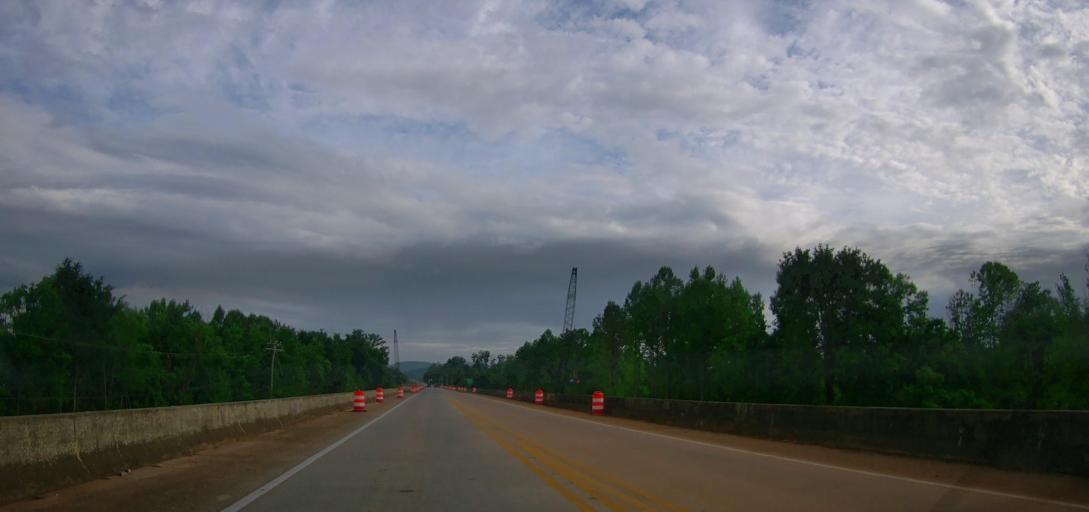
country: US
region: Alabama
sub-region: Calhoun County
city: Oxford
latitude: 33.6061
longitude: -85.7862
